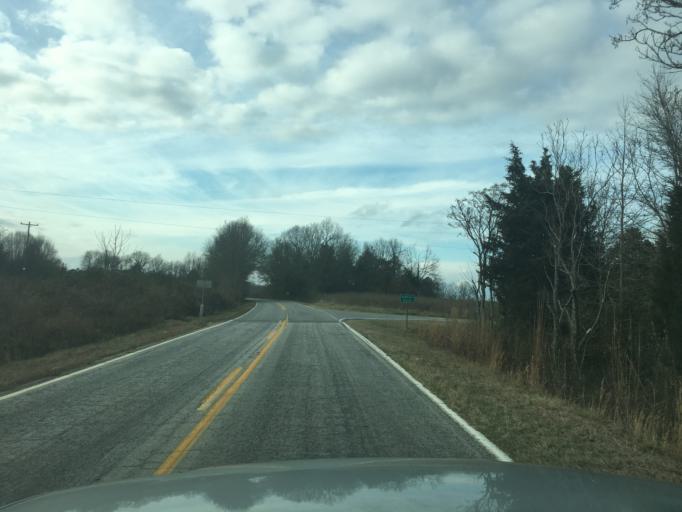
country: US
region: South Carolina
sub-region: Abbeville County
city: Lake Secession
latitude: 34.3571
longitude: -82.5083
